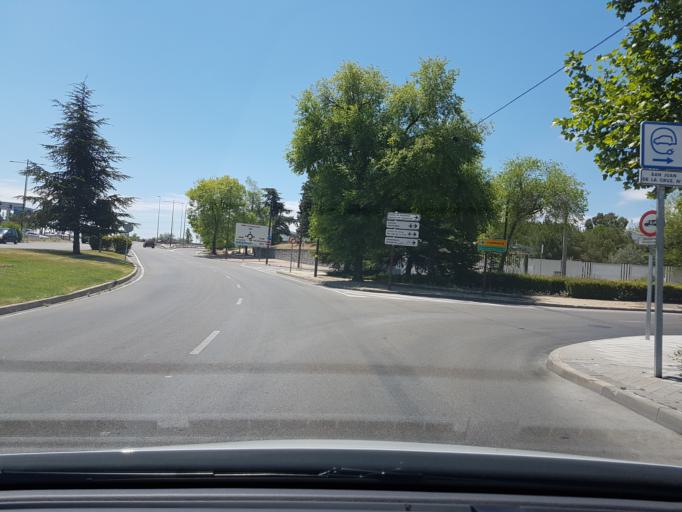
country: ES
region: Madrid
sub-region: Provincia de Madrid
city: Pozuelo de Alarcon
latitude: 40.4308
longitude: -3.8116
